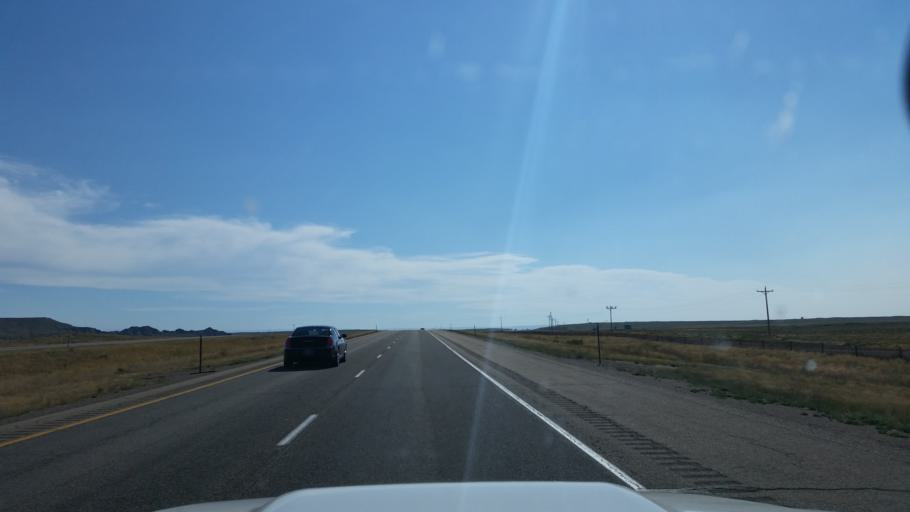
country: US
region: Wyoming
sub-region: Uinta County
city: Lyman
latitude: 41.4402
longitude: -110.0928
